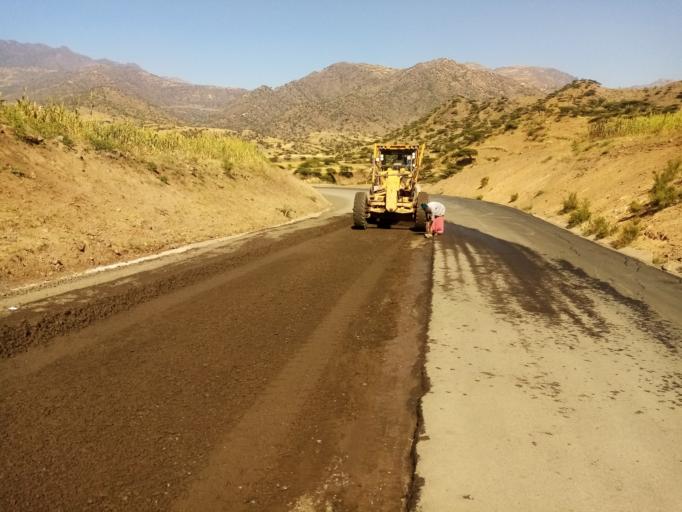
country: ET
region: Amhara
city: Lalibela
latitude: 12.2515
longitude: 39.0333
